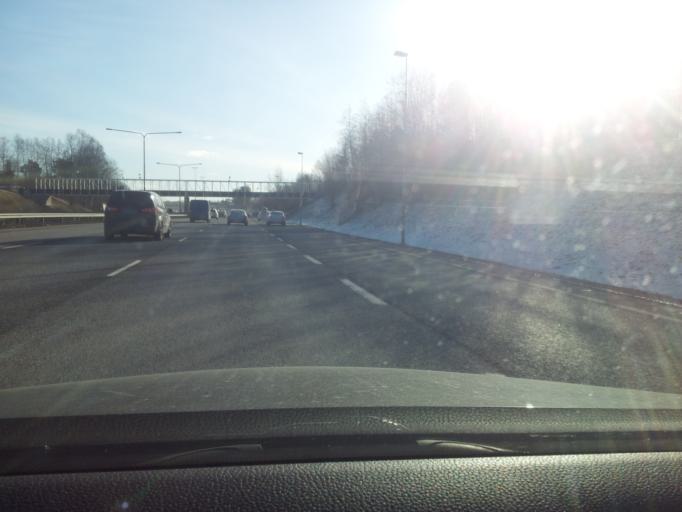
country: FI
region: Uusimaa
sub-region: Helsinki
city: Koukkuniemi
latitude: 60.1686
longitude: 24.7864
